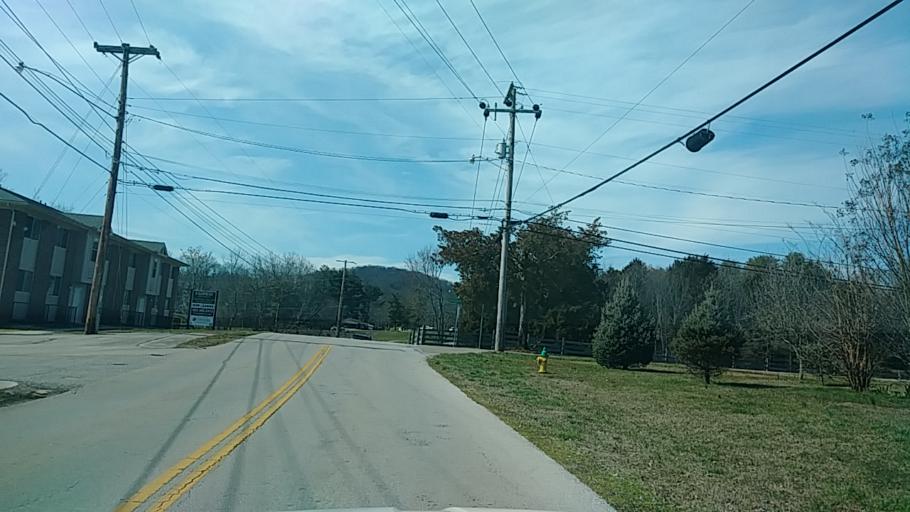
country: US
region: Tennessee
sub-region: Hamblen County
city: Morristown
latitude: 36.2127
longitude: -83.3313
